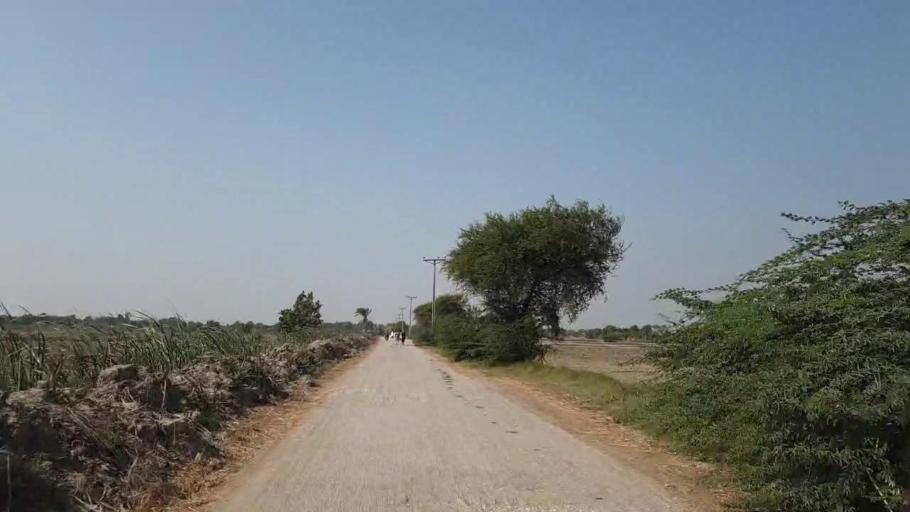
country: PK
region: Sindh
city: Bulri
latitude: 24.9567
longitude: 68.3351
